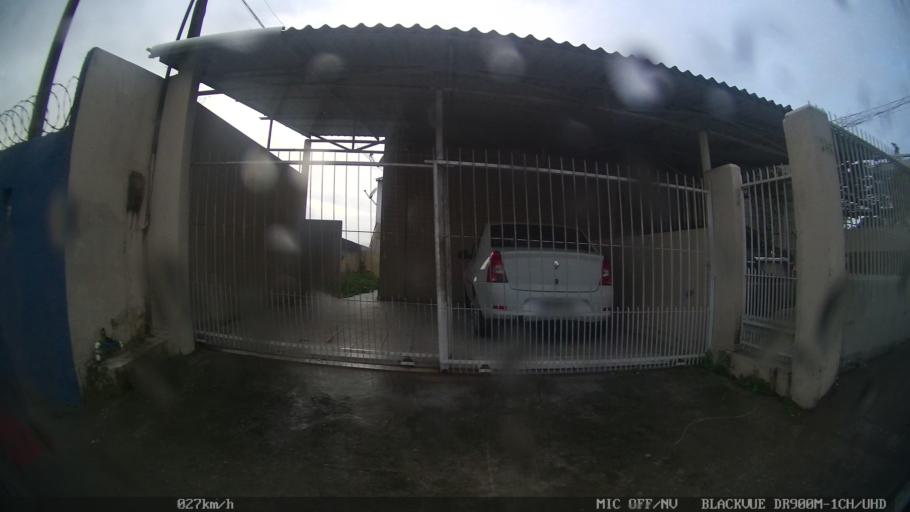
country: BR
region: Santa Catarina
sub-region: Sao Jose
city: Campinas
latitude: -27.6137
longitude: -48.6258
